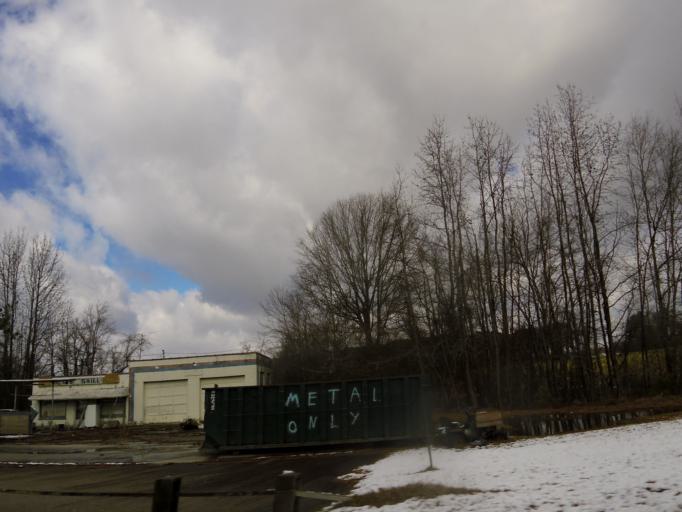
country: US
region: North Carolina
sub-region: Wilson County
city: Lucama
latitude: 35.7077
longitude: -78.0223
